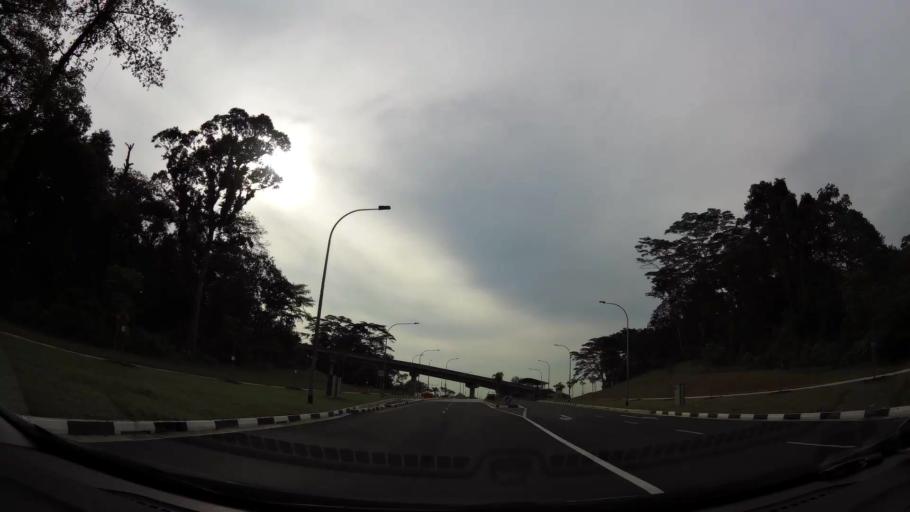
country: MY
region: Johor
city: Kampung Pasir Gudang Baru
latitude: 1.4163
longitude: 103.9090
